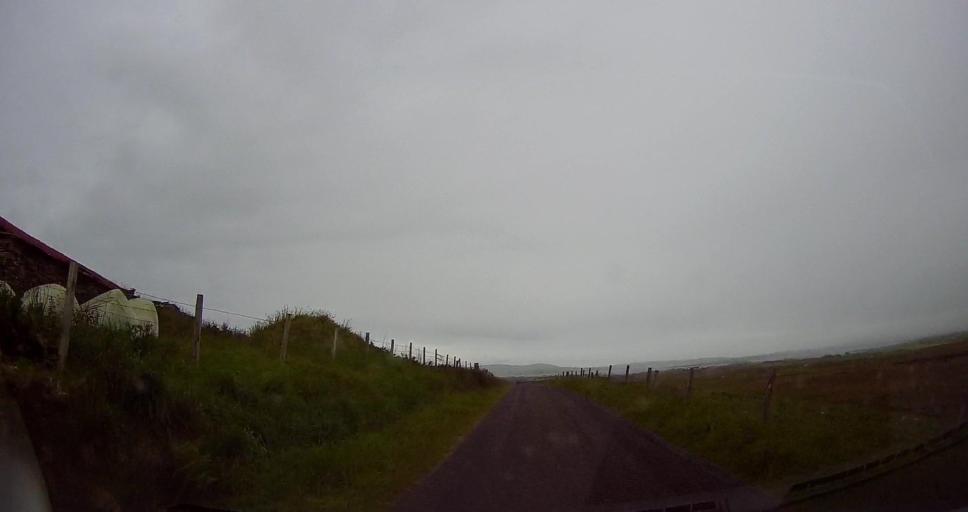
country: GB
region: Scotland
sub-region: Orkney Islands
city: Stromness
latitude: 58.9775
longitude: -3.1675
